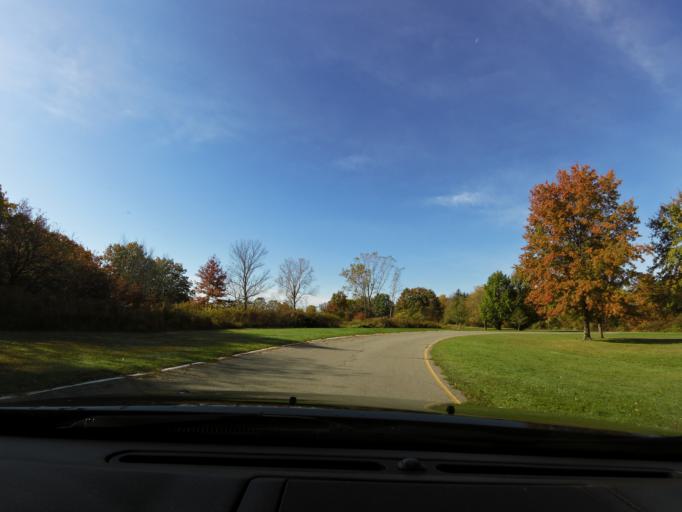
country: US
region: New York
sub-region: Livingston County
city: Mount Morris
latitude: 42.7317
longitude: -77.9157
